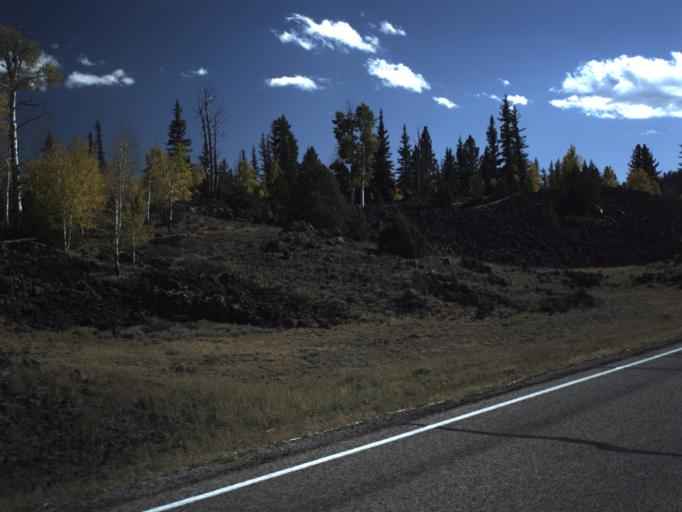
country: US
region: Utah
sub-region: Iron County
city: Parowan
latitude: 37.6786
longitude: -112.6665
